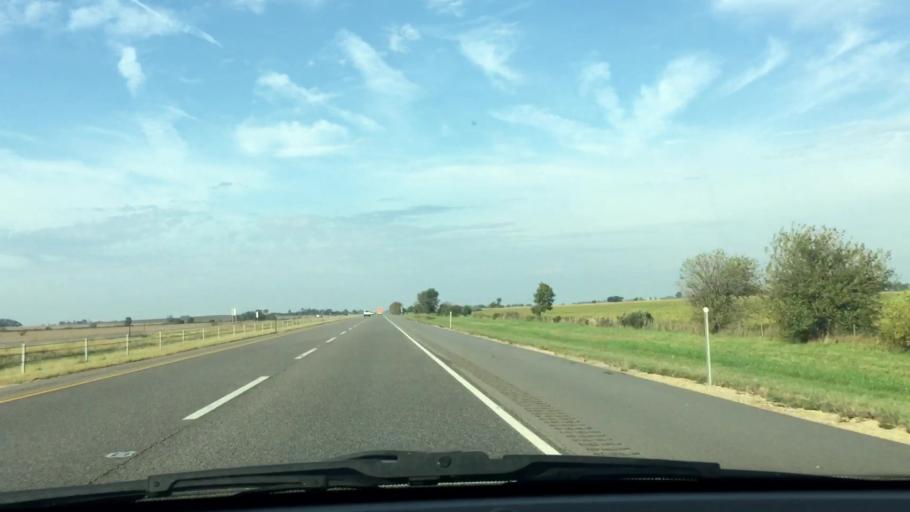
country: US
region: Illinois
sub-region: Ogle County
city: Rochelle
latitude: 41.8689
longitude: -89.1702
